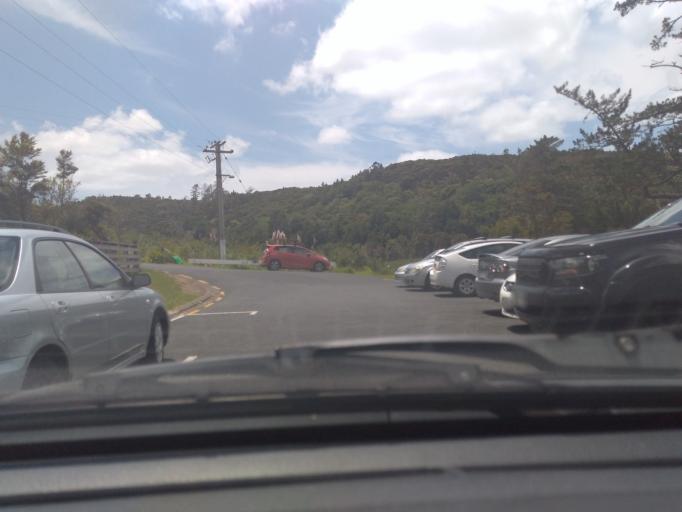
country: NZ
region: Auckland
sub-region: Auckland
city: Rothesay Bay
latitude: -36.6740
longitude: 174.7055
